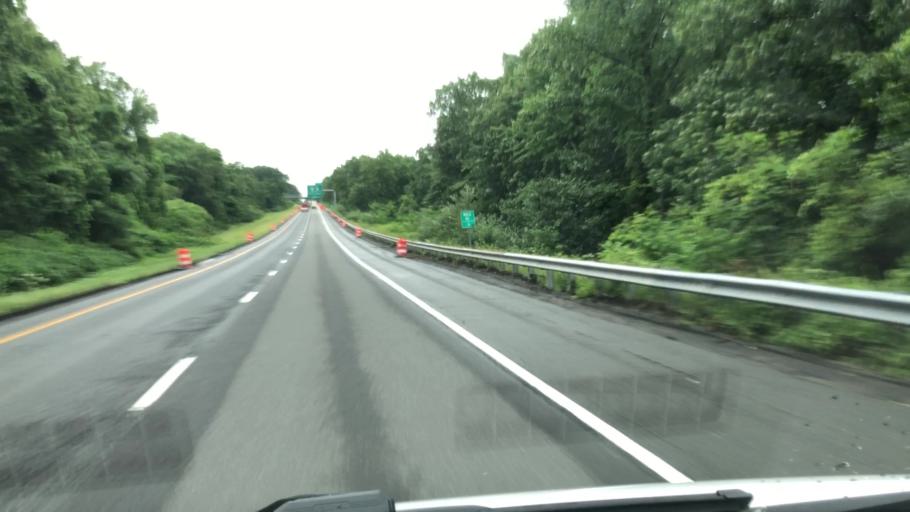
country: US
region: Massachusetts
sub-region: Franklin County
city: Greenfield
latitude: 42.5647
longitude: -72.6200
